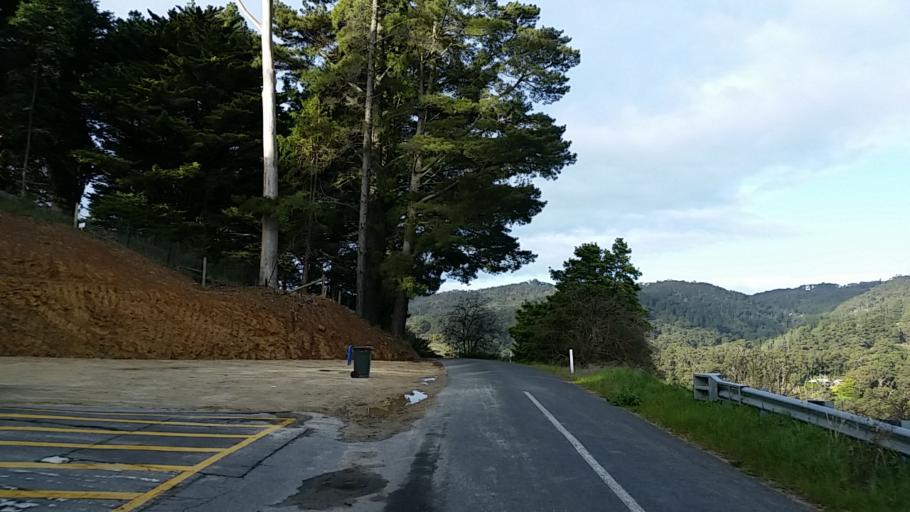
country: AU
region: South Australia
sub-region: Adelaide Hills
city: Bridgewater
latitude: -34.9395
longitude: 138.7655
